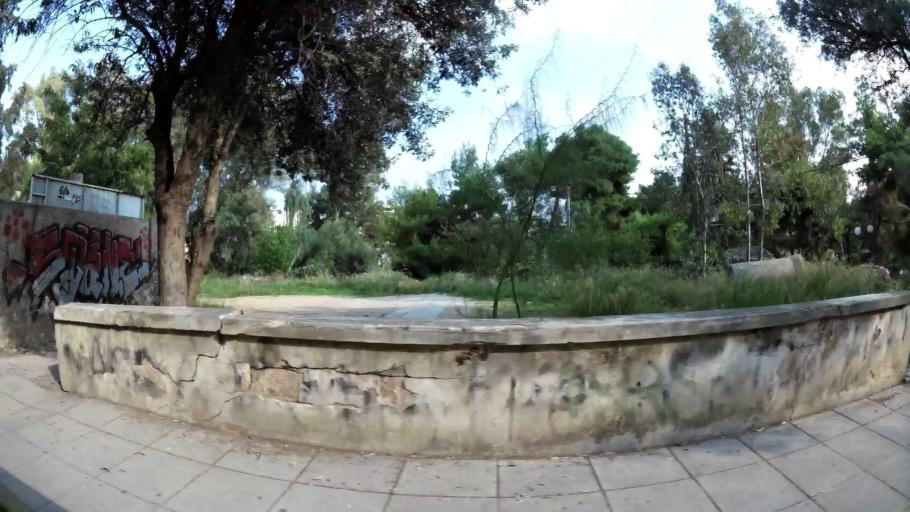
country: GR
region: Attica
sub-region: Nomarchia Athinas
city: Nea Filadelfeia
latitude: 38.0350
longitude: 23.7413
